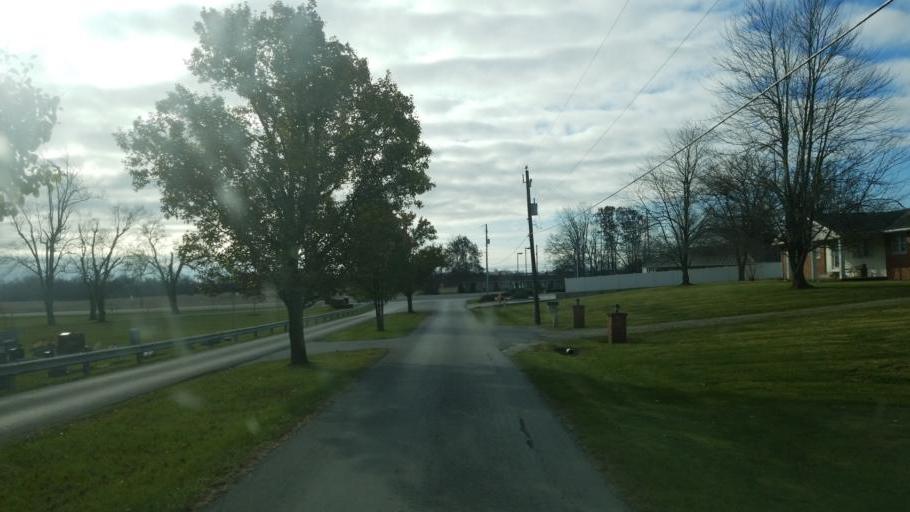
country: US
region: Ohio
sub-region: Hardin County
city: Kenton
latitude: 40.6459
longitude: -83.5905
